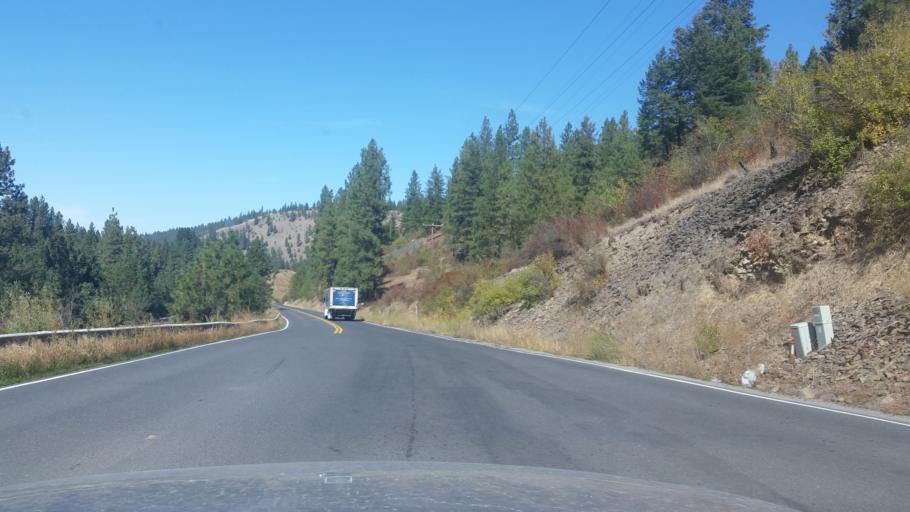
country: US
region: Washington
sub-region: Spokane County
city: Spokane
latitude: 47.6075
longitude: -117.4328
